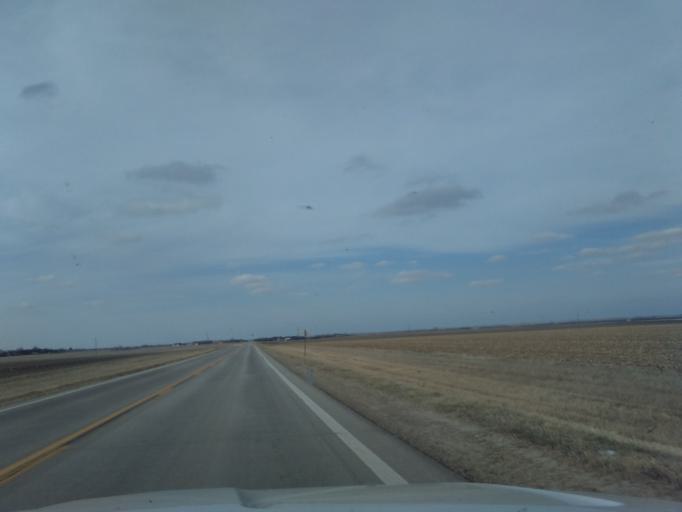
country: US
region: Nebraska
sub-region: Saline County
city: Wilber
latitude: 40.3177
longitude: -96.9162
